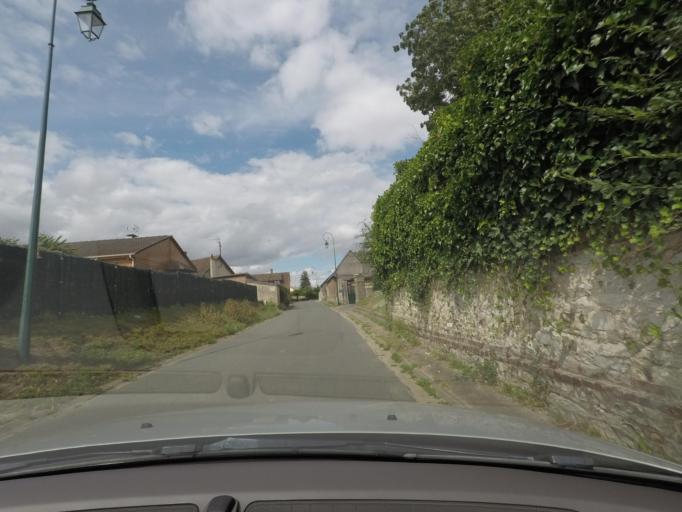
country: FR
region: Haute-Normandie
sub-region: Departement de l'Eure
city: Les Andelys
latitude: 49.1955
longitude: 1.4636
